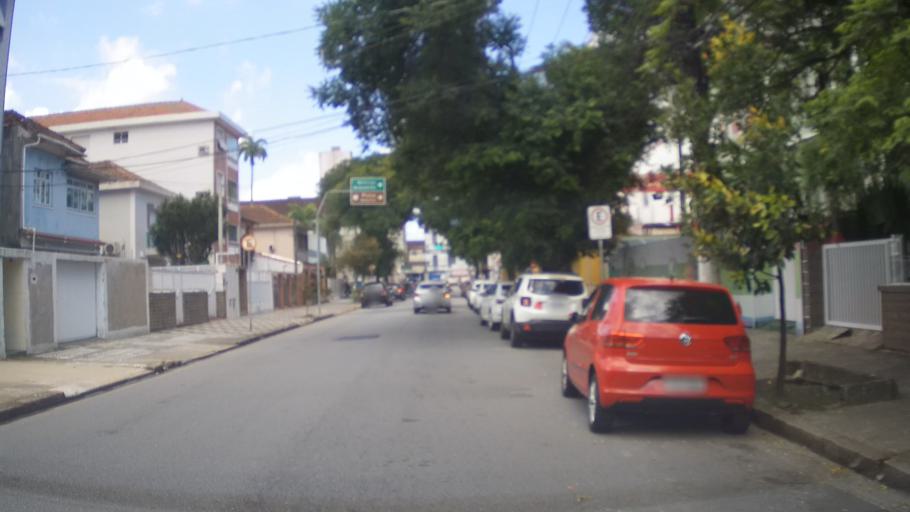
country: BR
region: Sao Paulo
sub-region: Santos
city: Santos
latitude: -23.9561
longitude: -46.3327
